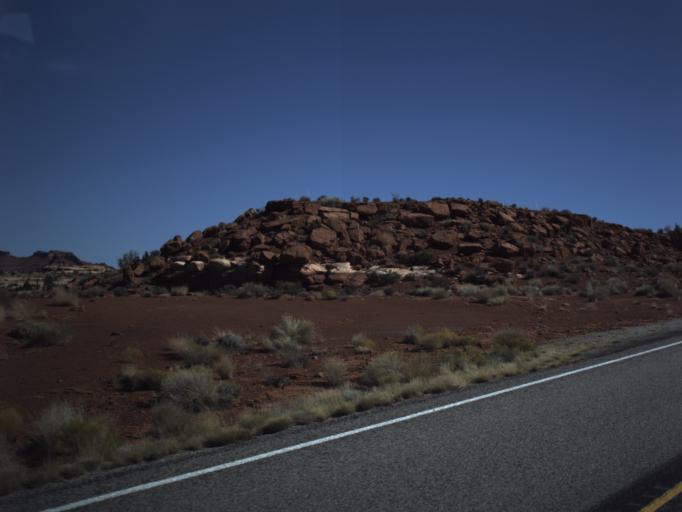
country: US
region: Utah
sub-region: San Juan County
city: Blanding
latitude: 37.8103
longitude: -110.3340
